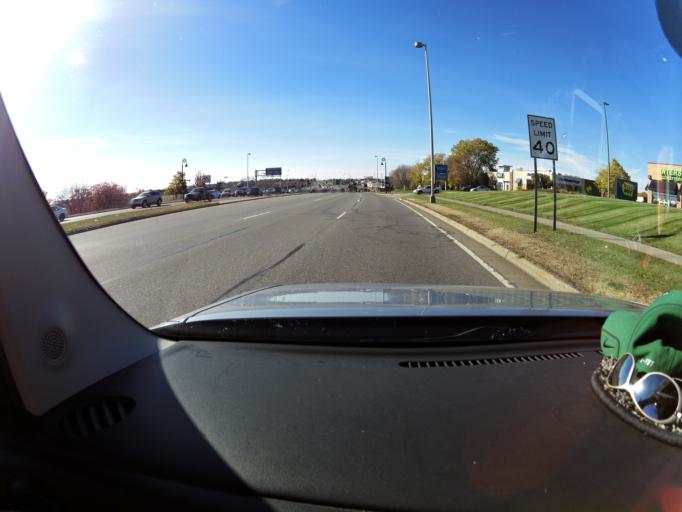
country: US
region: Minnesota
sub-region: Dakota County
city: Burnsville
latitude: 44.7464
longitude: -93.2855
